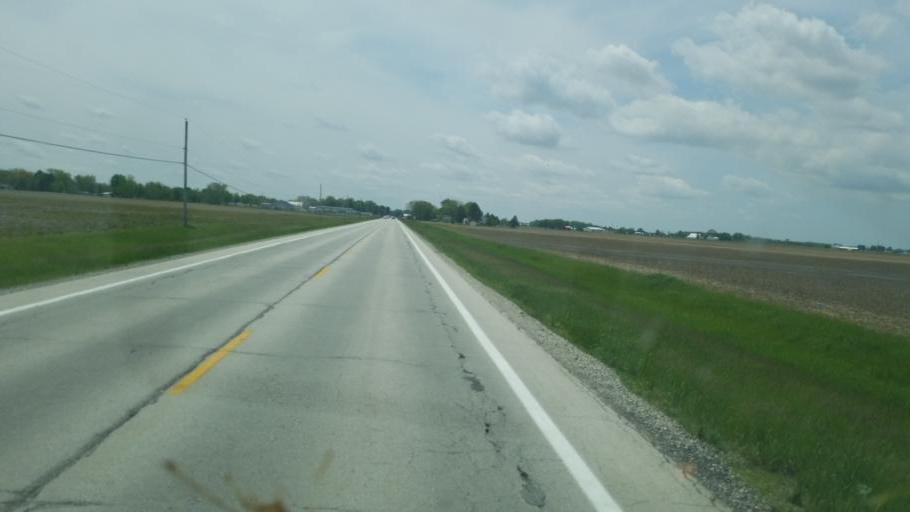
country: US
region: Ohio
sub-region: Sandusky County
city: Fremont
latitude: 41.4273
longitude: -83.0801
